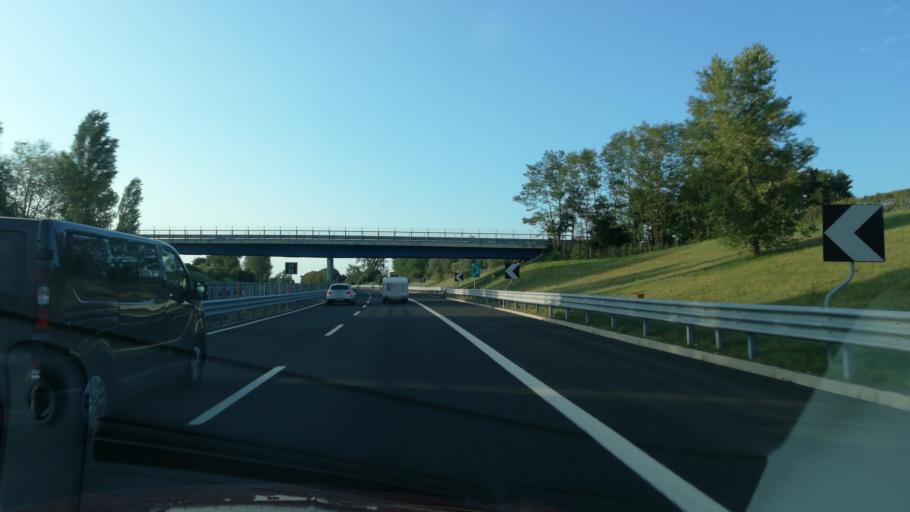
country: IT
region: Friuli Venezia Giulia
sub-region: Provincia di Udine
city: Pagnacco
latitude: 46.1403
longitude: 13.1759
